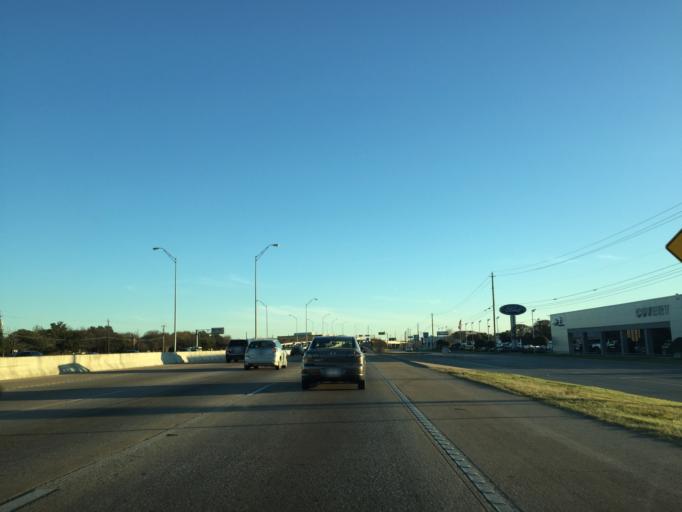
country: US
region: Texas
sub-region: Williamson County
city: Jollyville
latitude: 30.4136
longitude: -97.7461
